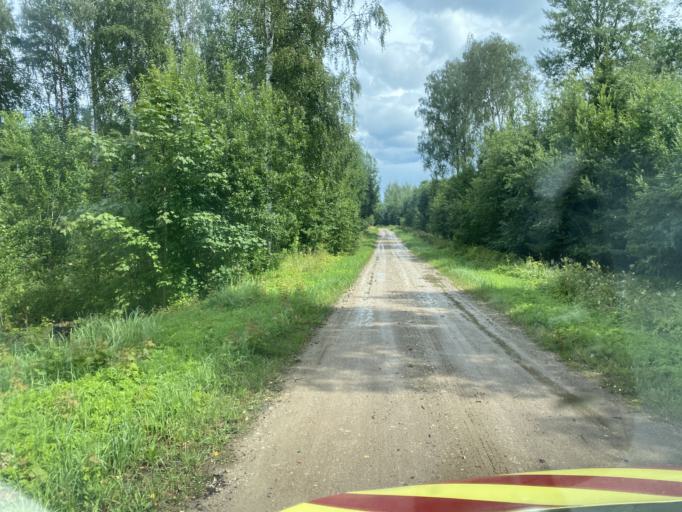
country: EE
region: Valgamaa
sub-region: Torva linn
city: Torva
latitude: 58.0959
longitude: 25.9952
